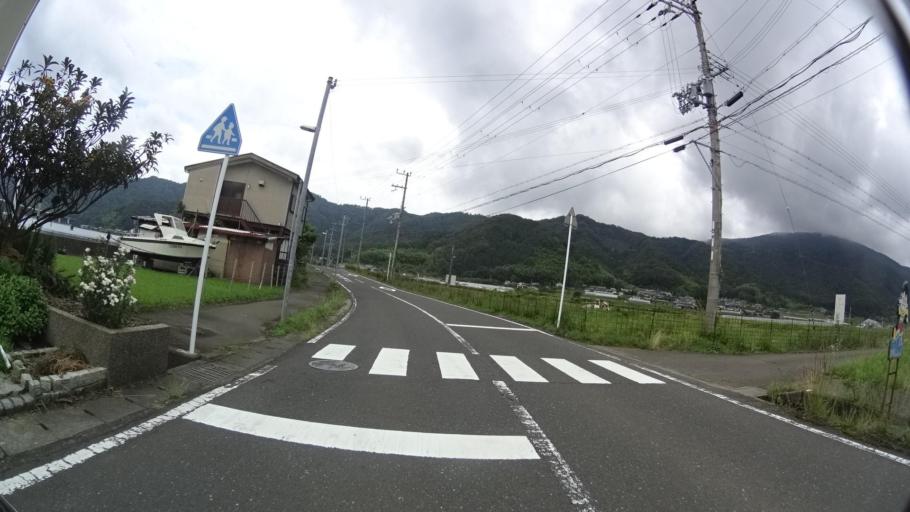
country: JP
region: Kyoto
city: Maizuru
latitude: 35.5066
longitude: 135.3785
